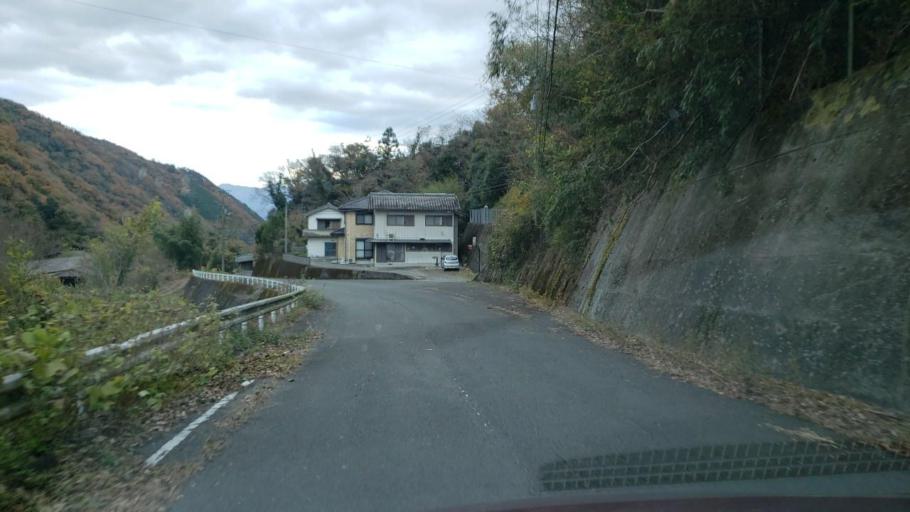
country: JP
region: Tokushima
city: Wakimachi
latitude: 34.1240
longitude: 134.2261
